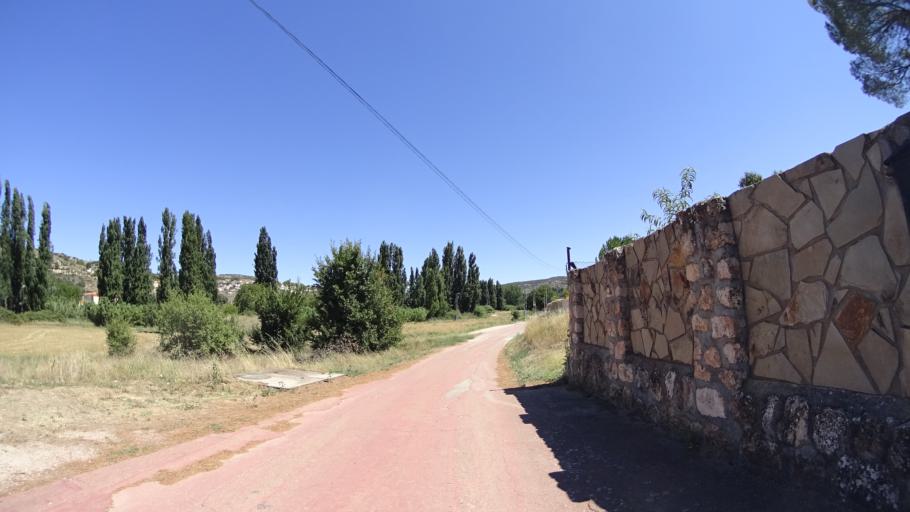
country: ES
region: Madrid
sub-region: Provincia de Madrid
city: Carabana
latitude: 40.2763
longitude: -3.2124
